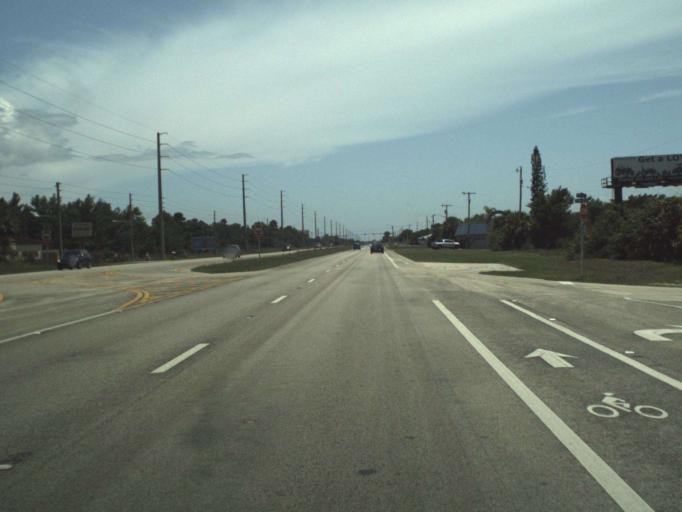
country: US
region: Florida
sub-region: Saint Lucie County
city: Lakewood Park
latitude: 27.5256
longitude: -80.3583
